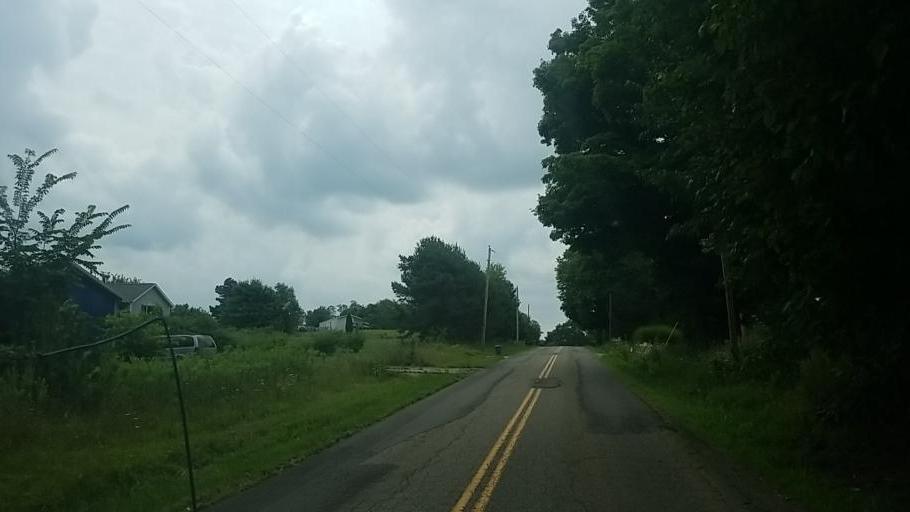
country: US
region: Ohio
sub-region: Knox County
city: Mount Vernon
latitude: 40.3410
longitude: -82.4568
